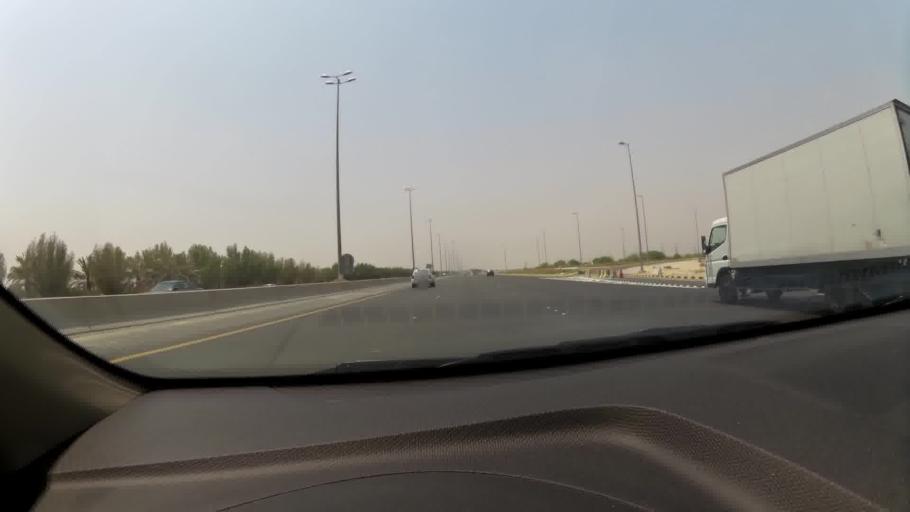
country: KW
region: Muhafazat al Jahra'
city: Al Jahra'
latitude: 29.3185
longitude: 47.7624
